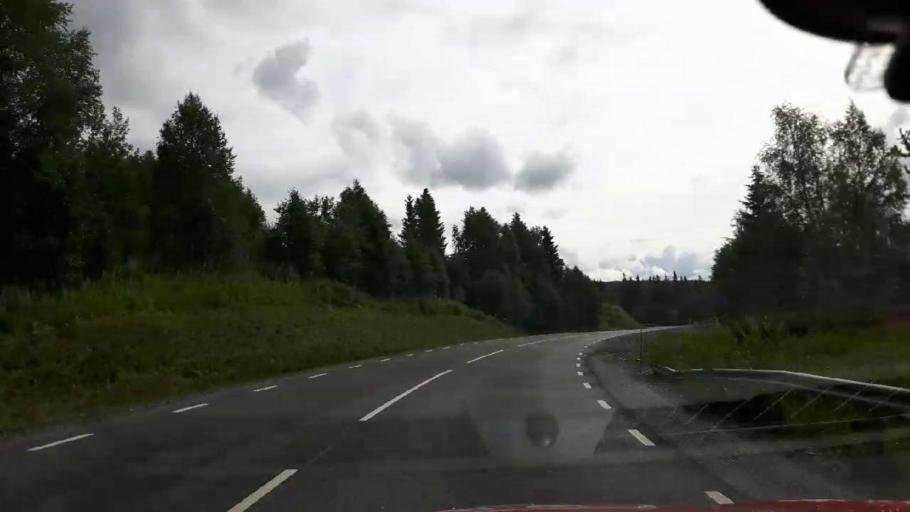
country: NO
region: Nord-Trondelag
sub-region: Lierne
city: Sandvika
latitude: 64.6503
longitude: 14.1377
